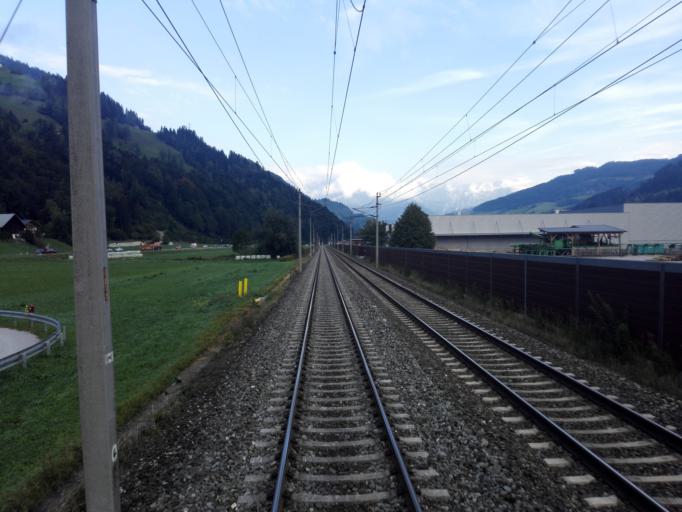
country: AT
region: Salzburg
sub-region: Politischer Bezirk Sankt Johann im Pongau
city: Sankt Johann im Pongau
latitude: 47.3688
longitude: 13.2069
